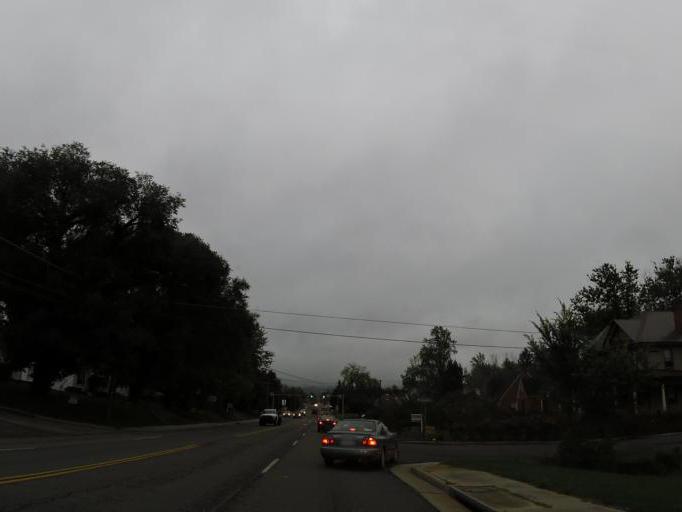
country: US
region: Virginia
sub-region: Wythe County
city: Wytheville
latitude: 36.9521
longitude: -81.0894
